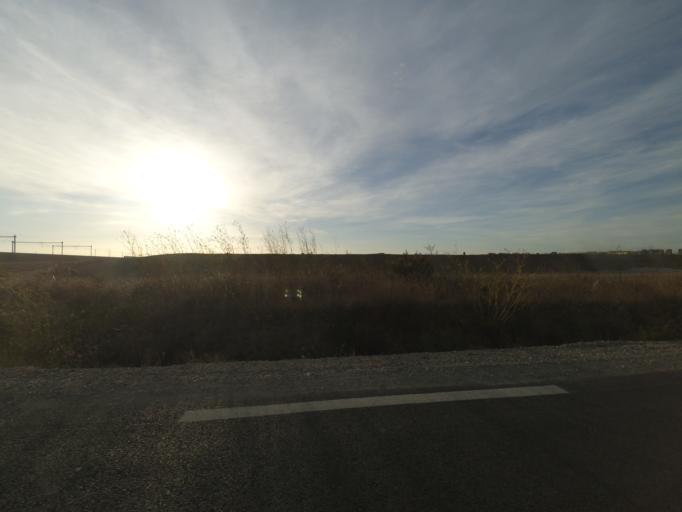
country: FR
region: Languedoc-Roussillon
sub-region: Departement du Gard
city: Codognan
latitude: 43.7137
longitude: 4.2278
